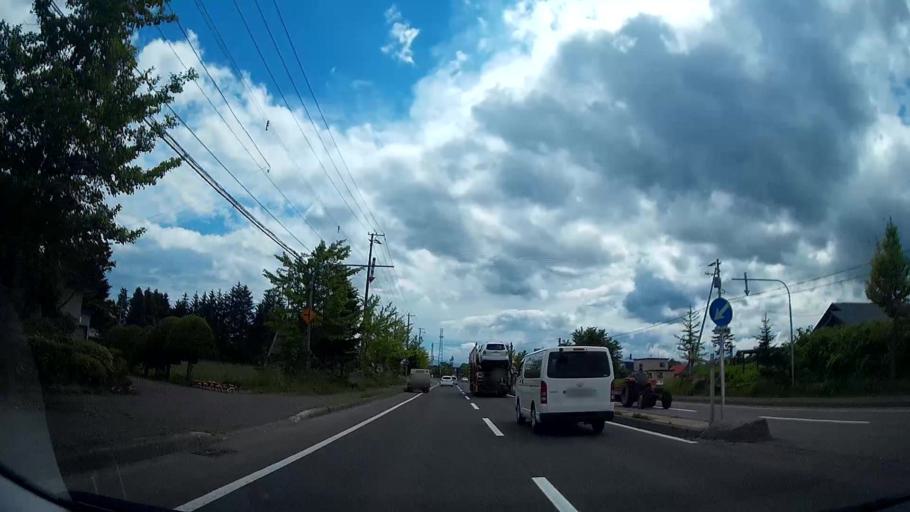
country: JP
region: Hokkaido
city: Kitahiroshima
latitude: 42.8750
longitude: 141.5635
